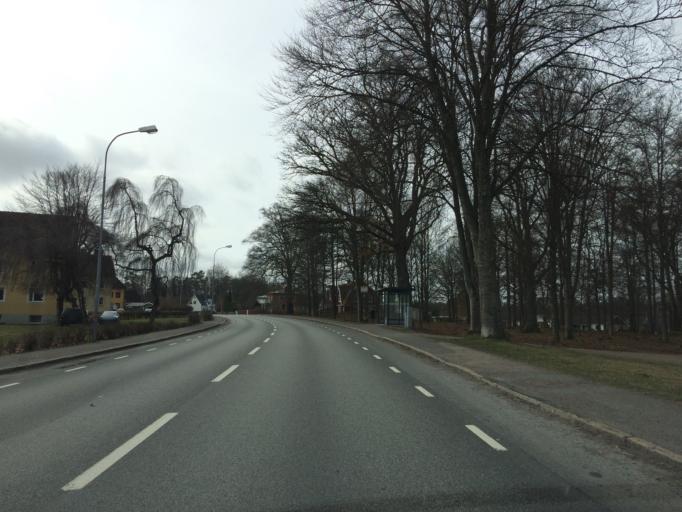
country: SE
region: Skane
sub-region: Osby Kommun
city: Lonsboda
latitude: 56.3953
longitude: 14.3144
